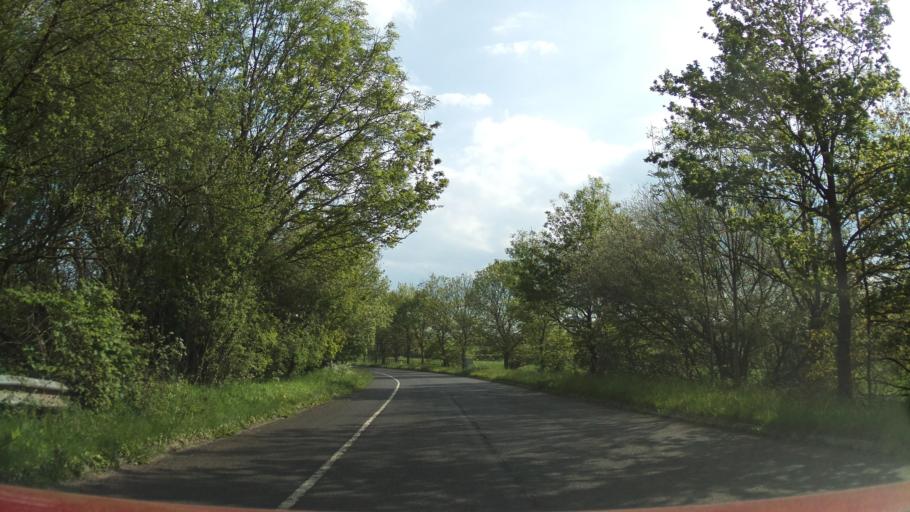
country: GB
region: England
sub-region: Wiltshire
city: Chippenham
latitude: 51.5132
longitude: -2.0787
